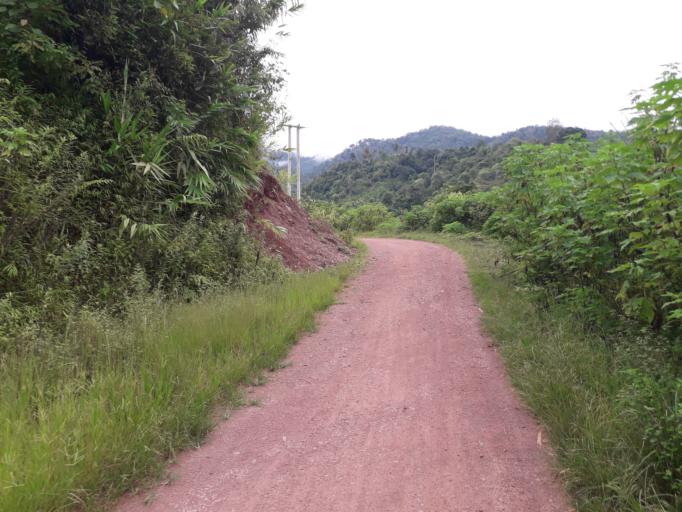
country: CN
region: Yunnan
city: Menglie
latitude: 22.2461
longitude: 101.6096
